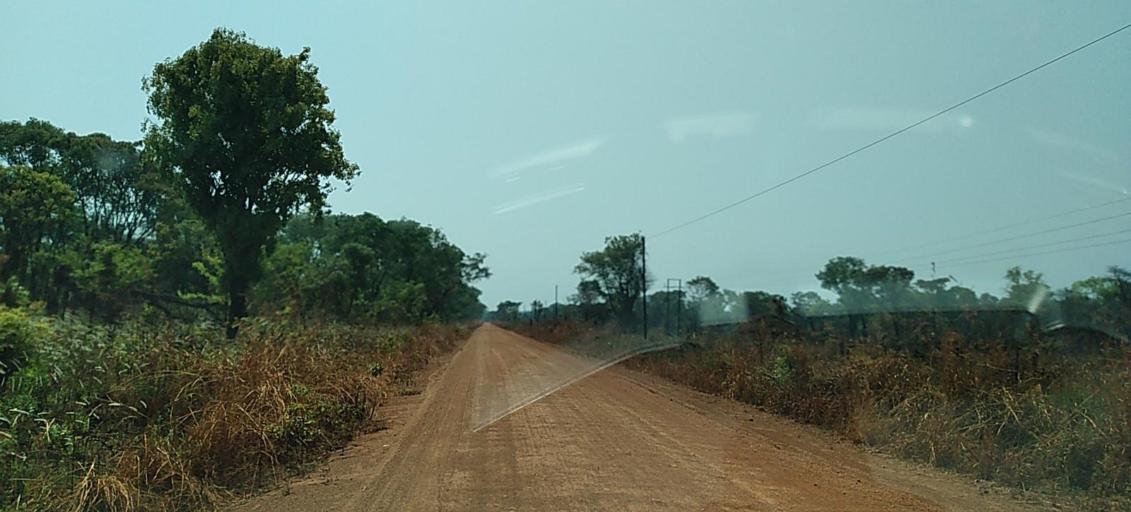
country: ZM
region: North-Western
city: Kansanshi
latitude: -11.9962
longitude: 26.6543
